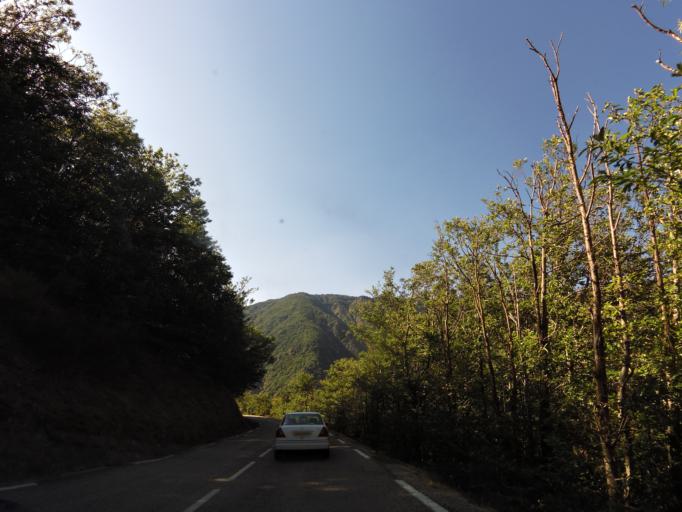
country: FR
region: Languedoc-Roussillon
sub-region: Departement du Gard
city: Valleraugue
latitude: 44.0916
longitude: 3.5782
